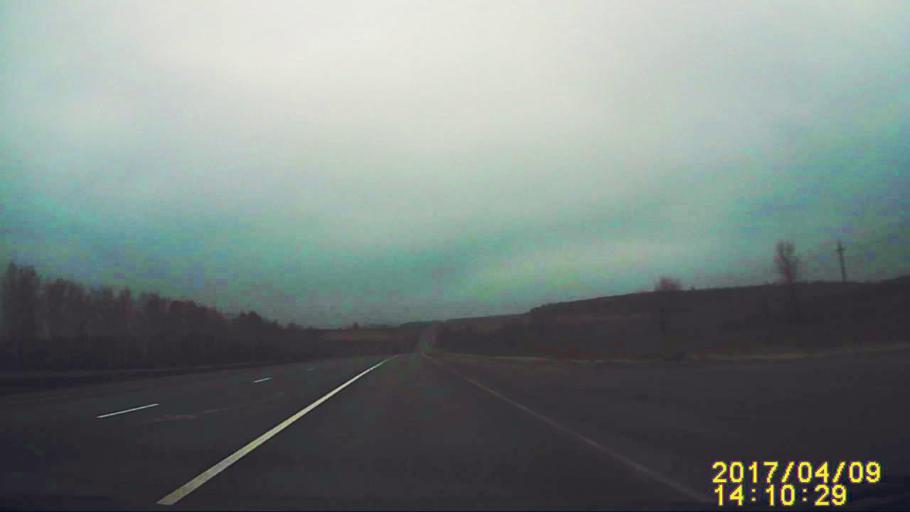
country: RU
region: Ulyanovsk
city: Krasnyy Gulyay
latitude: 54.0388
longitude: 48.2135
